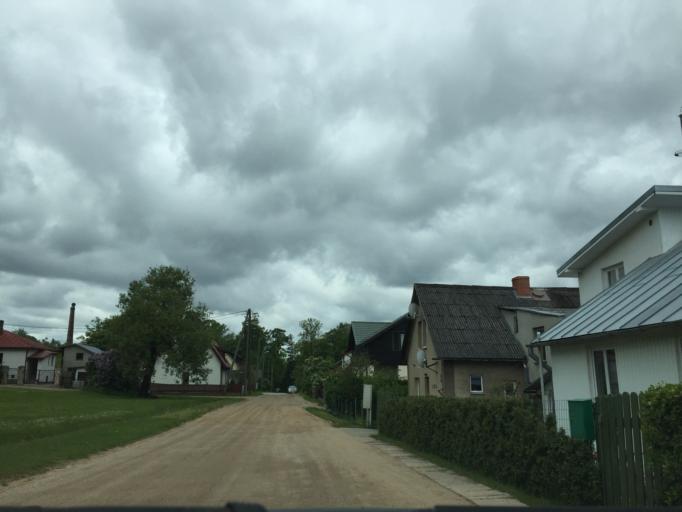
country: LV
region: Cesu Rajons
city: Cesis
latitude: 57.3170
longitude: 25.2728
